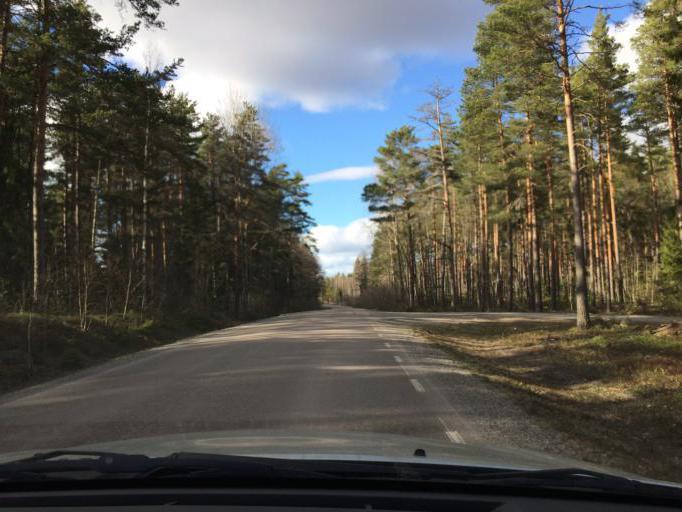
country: SE
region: Soedermanland
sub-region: Eskilstuna Kommun
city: Torshalla
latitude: 59.4215
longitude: 16.4348
